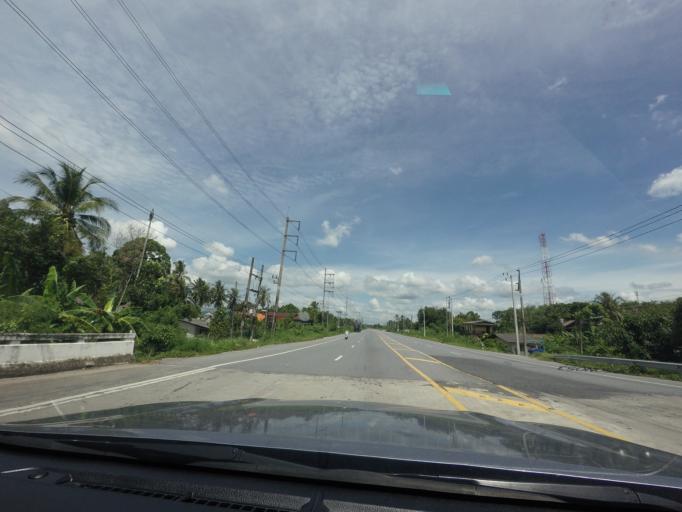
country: TH
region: Songkhla
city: Chana
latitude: 6.9878
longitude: 100.6783
